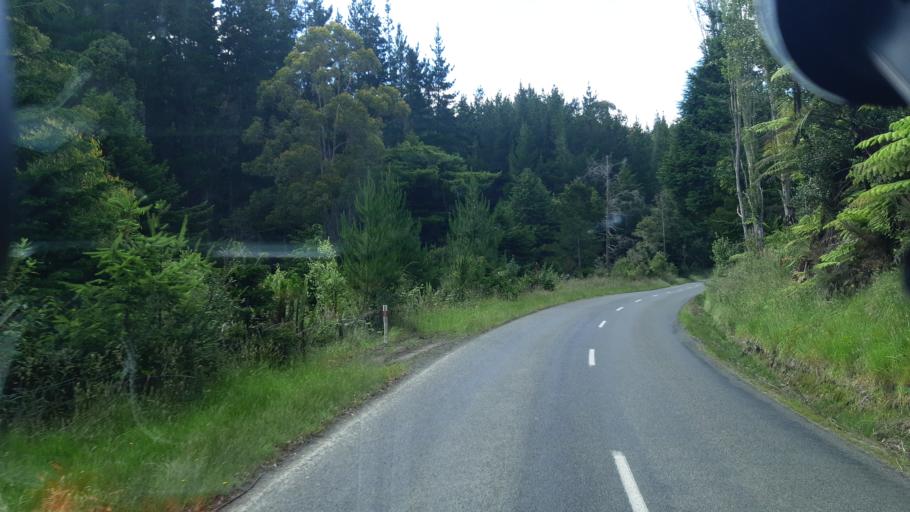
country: NZ
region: Manawatu-Wanganui
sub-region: Rangitikei District
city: Bulls
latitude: -39.9180
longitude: 175.5549
